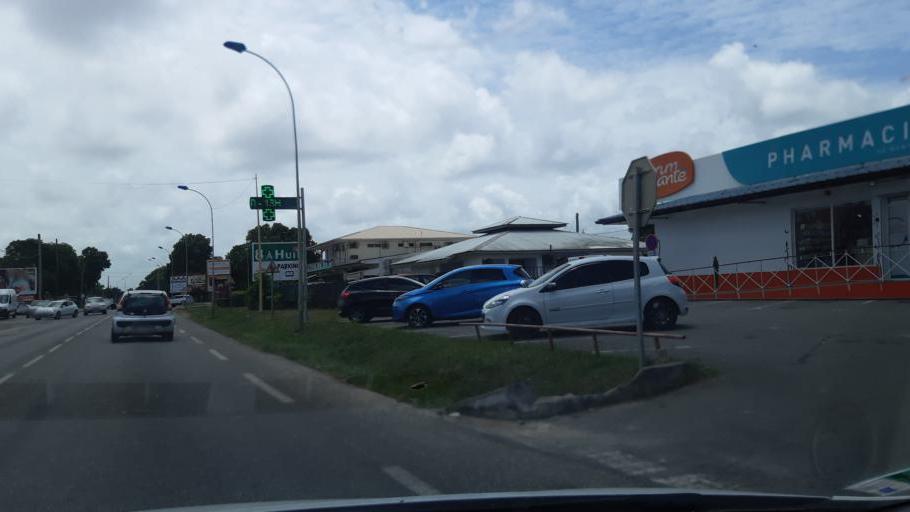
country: GF
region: Guyane
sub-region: Guyane
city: Remire-Montjoly
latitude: 4.9140
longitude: -52.2739
